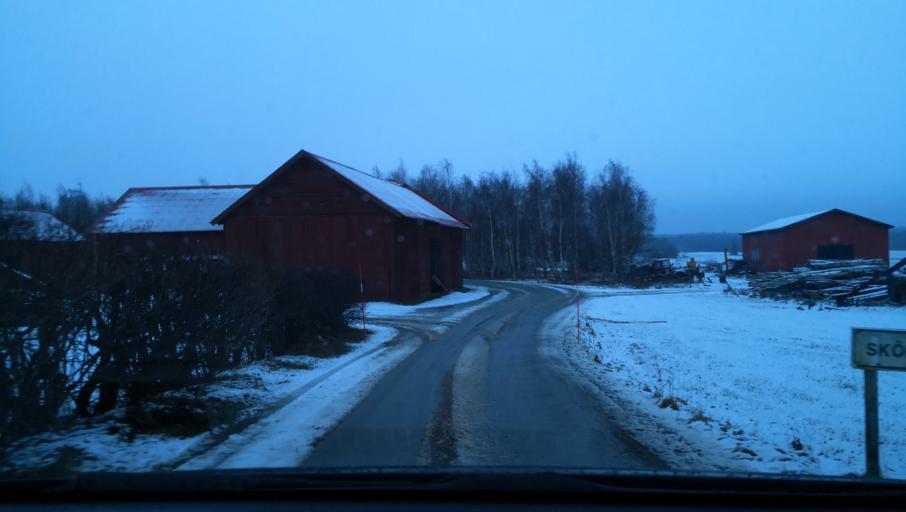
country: SE
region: Vaestmanland
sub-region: Kungsors Kommun
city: Kungsoer
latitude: 59.3942
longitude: 16.2123
